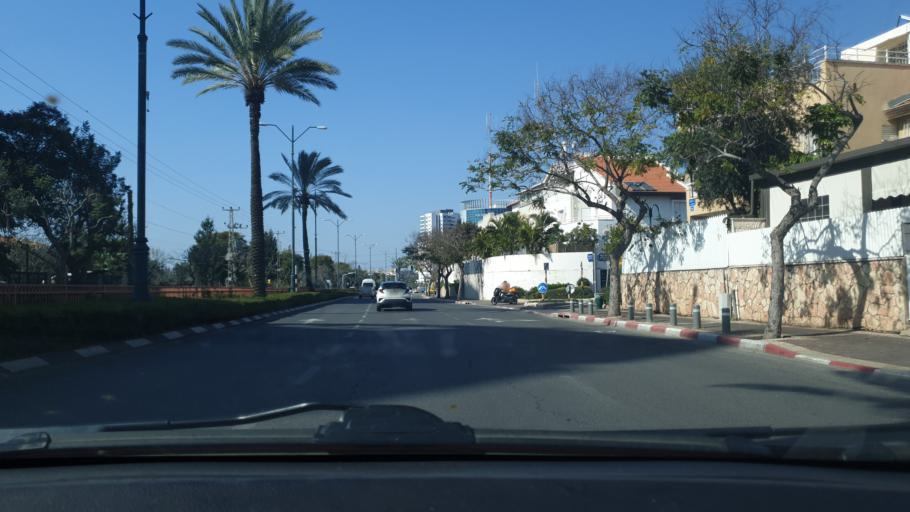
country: IL
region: Central District
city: Rishon LeZiyyon
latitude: 31.9725
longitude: 34.7979
